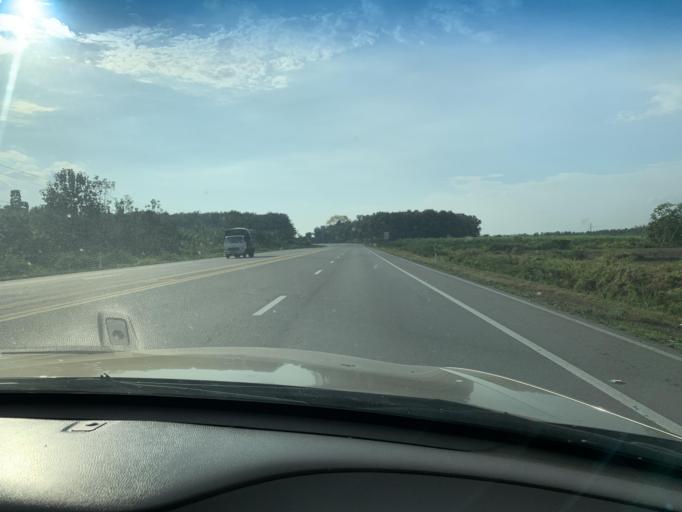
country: EC
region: Guayas
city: Coronel Marcelino Mariduena
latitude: -2.2825
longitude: -79.5172
